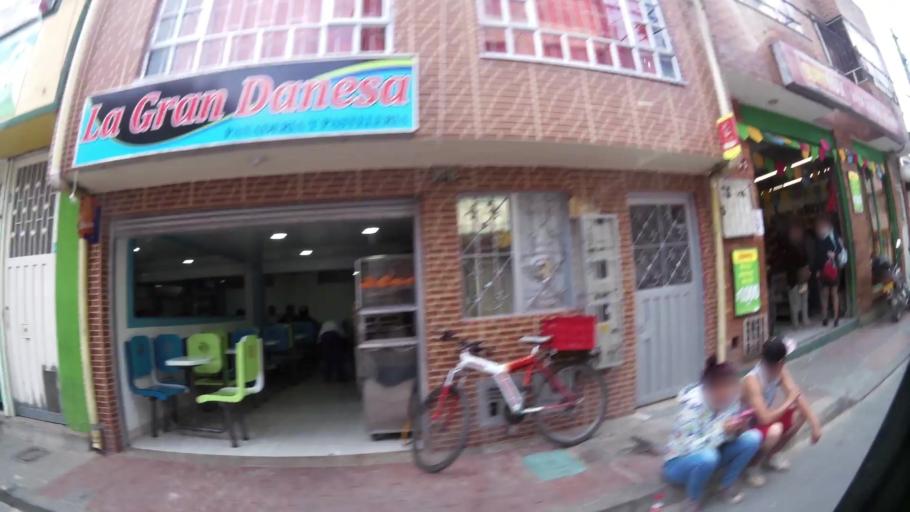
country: CO
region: Cundinamarca
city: Cota
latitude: 4.7268
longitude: -74.0977
